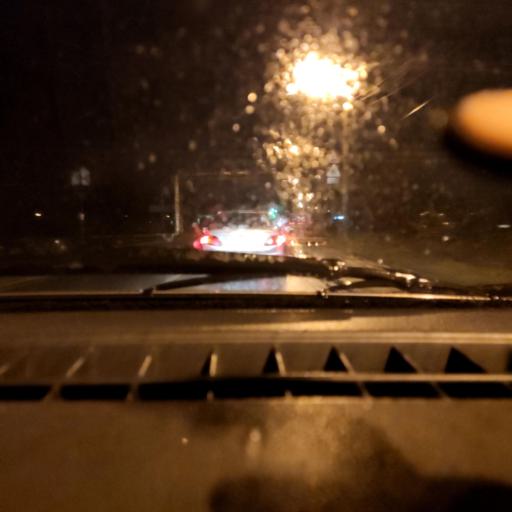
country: RU
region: Bashkortostan
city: Ufa
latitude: 54.8119
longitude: 56.1614
